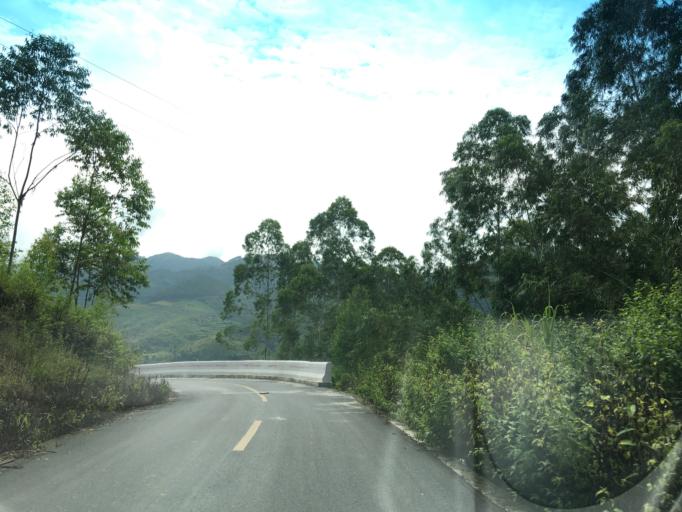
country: CN
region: Guangxi Zhuangzu Zizhiqu
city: Xinzhou
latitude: 24.8189
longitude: 105.6479
